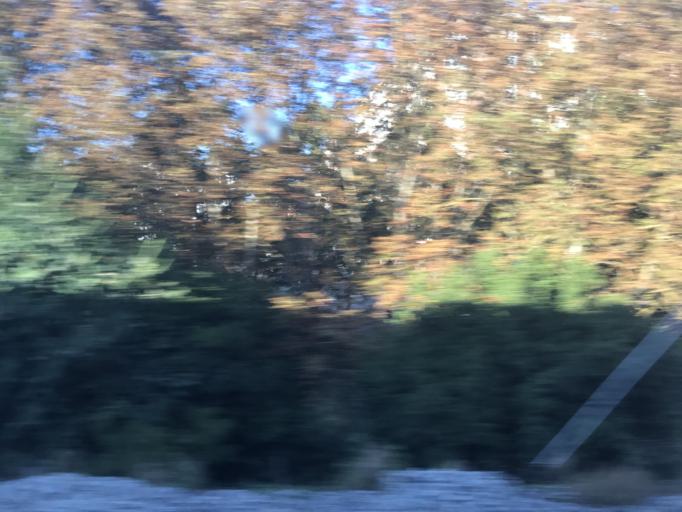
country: ES
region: Basque Country
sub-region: Provincia de Alava
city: Gasteiz / Vitoria
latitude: 42.8429
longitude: -2.6861
